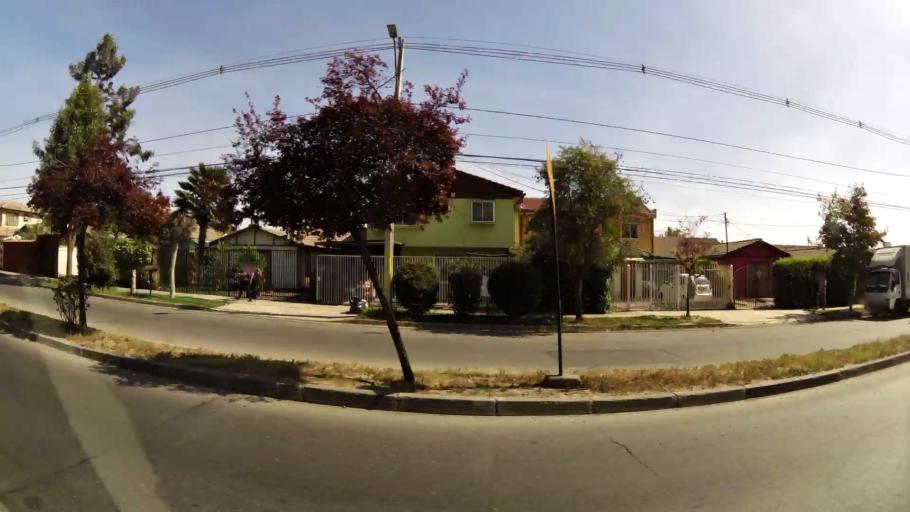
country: CL
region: Santiago Metropolitan
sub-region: Provincia de Cordillera
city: Puente Alto
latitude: -33.5778
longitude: -70.5526
